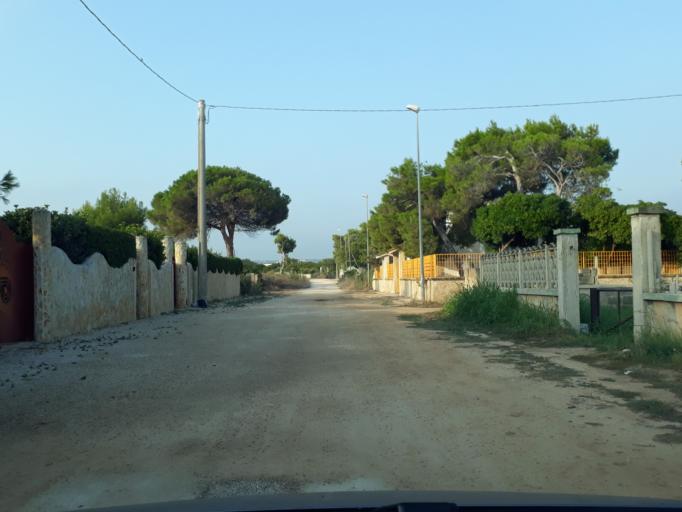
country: IT
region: Apulia
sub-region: Provincia di Brindisi
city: Carovigno
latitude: 40.7506
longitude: 17.7182
